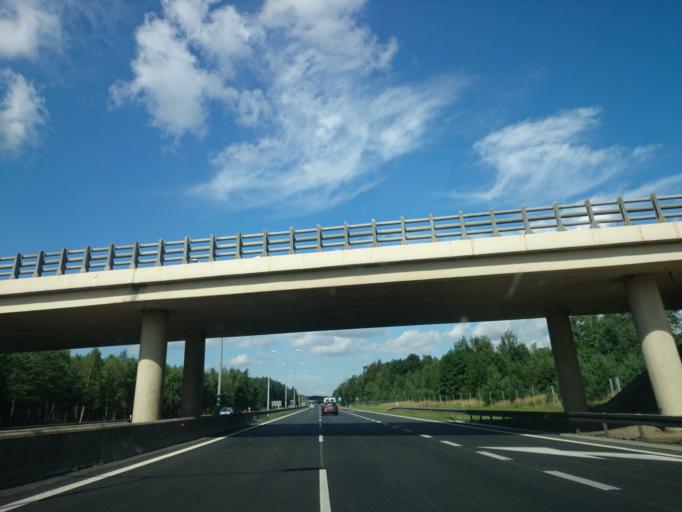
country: PL
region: Opole Voivodeship
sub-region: Powiat opolski
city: Dabrowa
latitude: 50.6621
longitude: 17.6954
